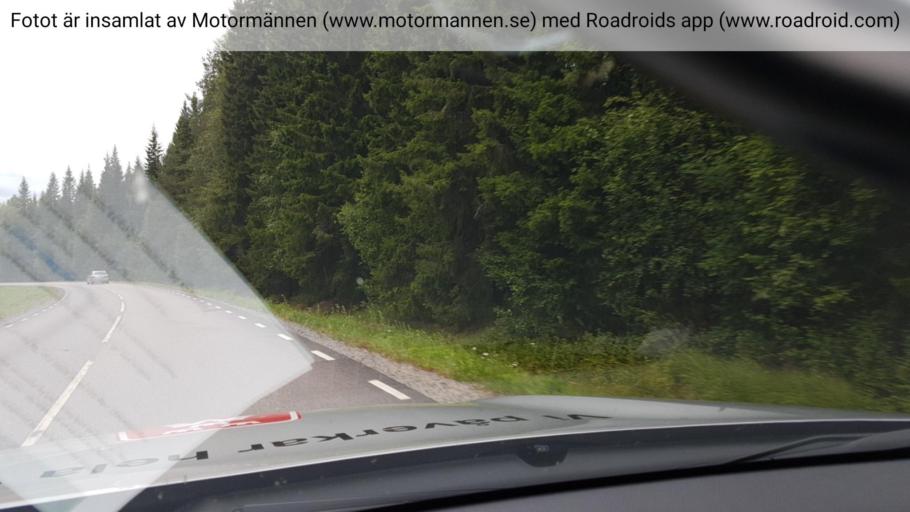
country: SE
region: Norrbotten
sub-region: Lulea Kommun
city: Gammelstad
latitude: 65.6569
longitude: 22.0412
